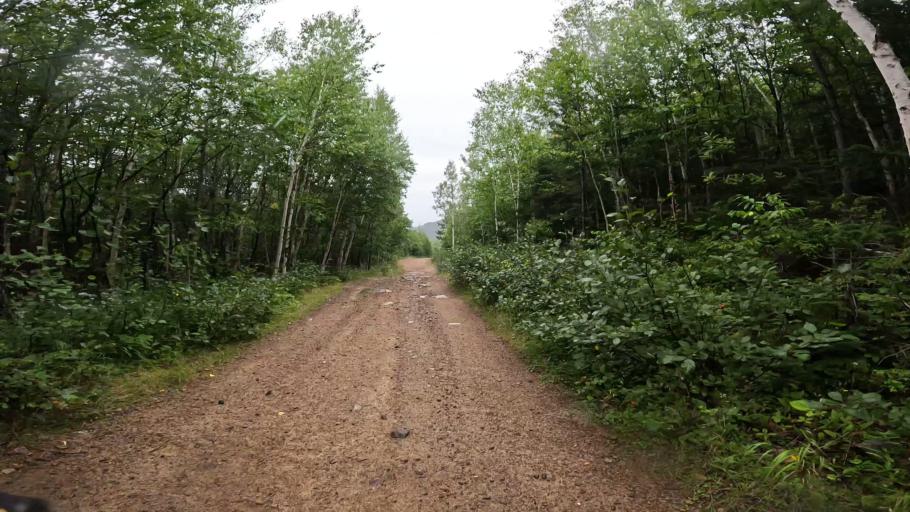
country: CA
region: Quebec
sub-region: Capitale-Nationale
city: Baie-Saint-Paul
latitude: 47.7918
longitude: -70.4885
